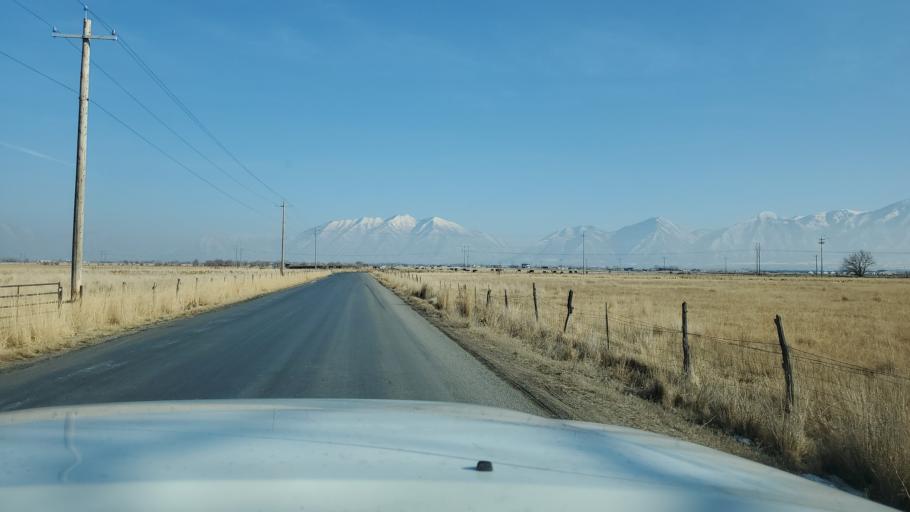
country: US
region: Utah
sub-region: Utah County
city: West Mountain
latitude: 40.0997
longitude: -111.7903
